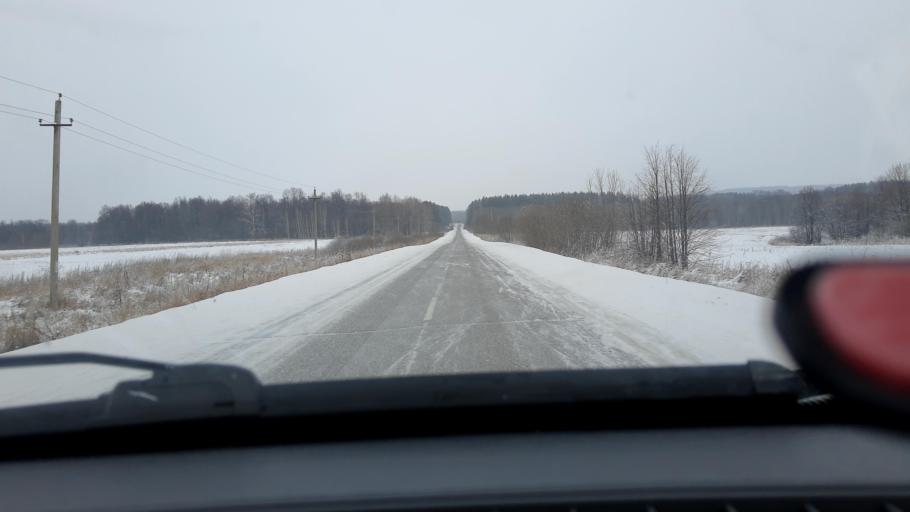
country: RU
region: Bashkortostan
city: Iglino
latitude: 54.6685
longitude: 56.4213
